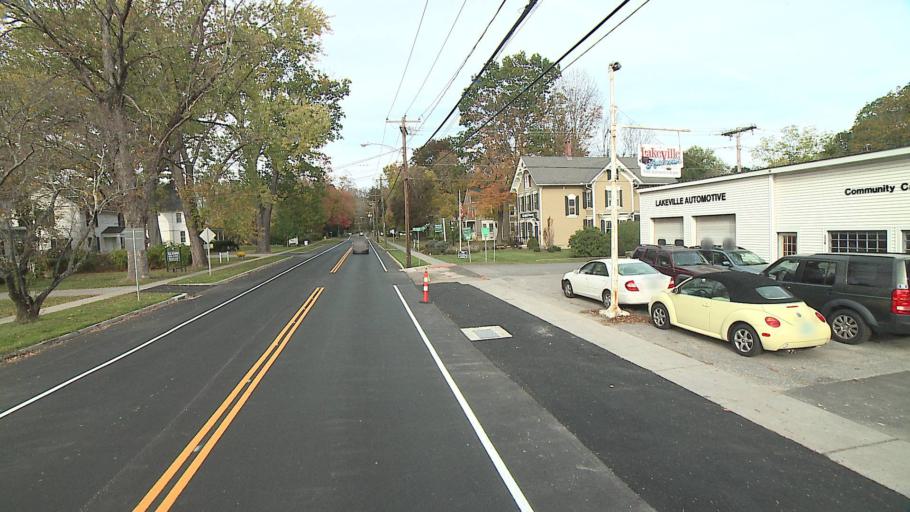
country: US
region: Connecticut
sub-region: Litchfield County
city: Canaan
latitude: 41.9659
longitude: -73.4399
